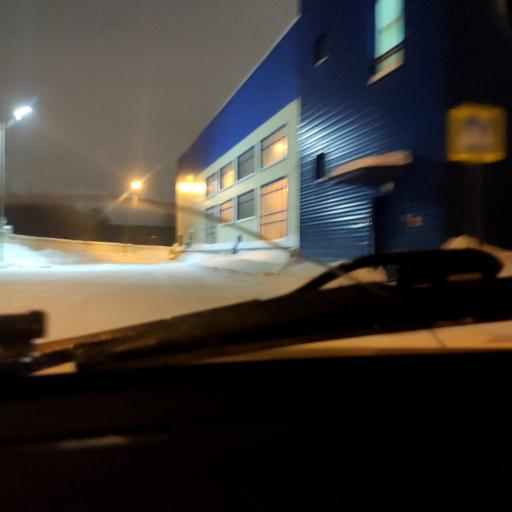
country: RU
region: Tatarstan
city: Staroye Arakchino
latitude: 55.8314
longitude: 49.0315
